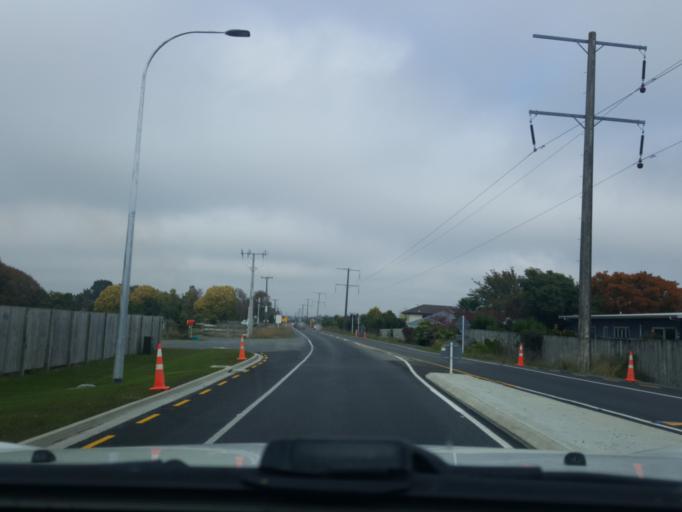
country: NZ
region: Waikato
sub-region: Hamilton City
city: Hamilton
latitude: -37.7330
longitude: 175.2874
